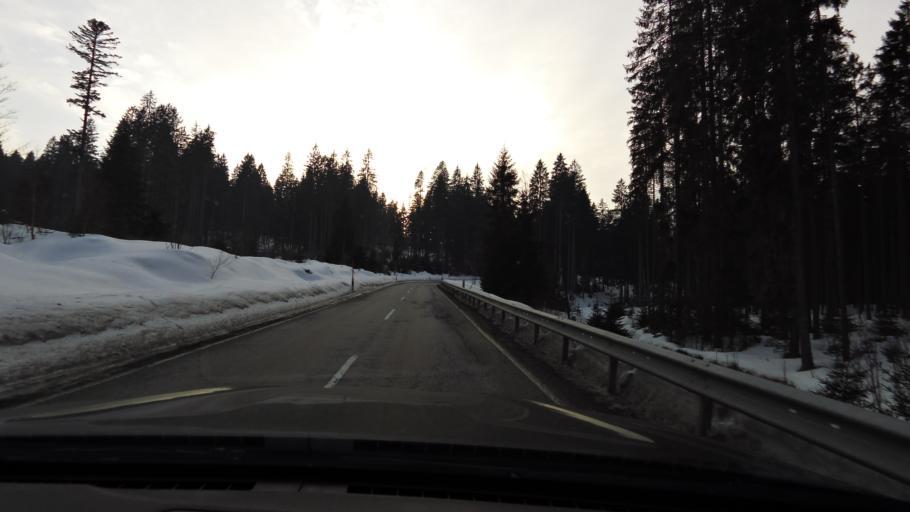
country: DE
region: Bavaria
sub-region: Lower Bavaria
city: Philippsreut
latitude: 48.8647
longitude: 13.7091
